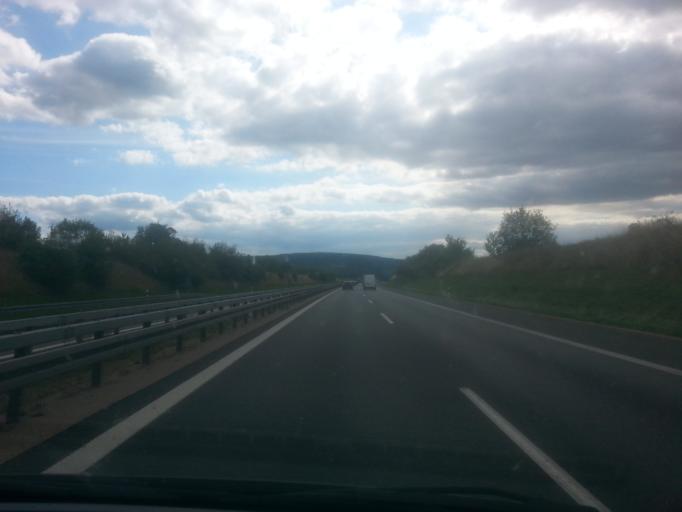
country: DE
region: Bavaria
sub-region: Upper Palatinate
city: Nabburg
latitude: 49.4503
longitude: 12.1923
